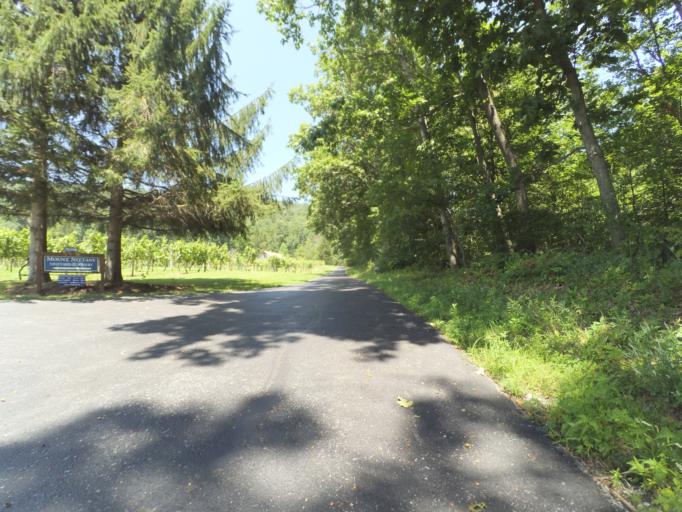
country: US
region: Pennsylvania
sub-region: Centre County
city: Boalsburg
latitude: 40.8091
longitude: -77.7691
